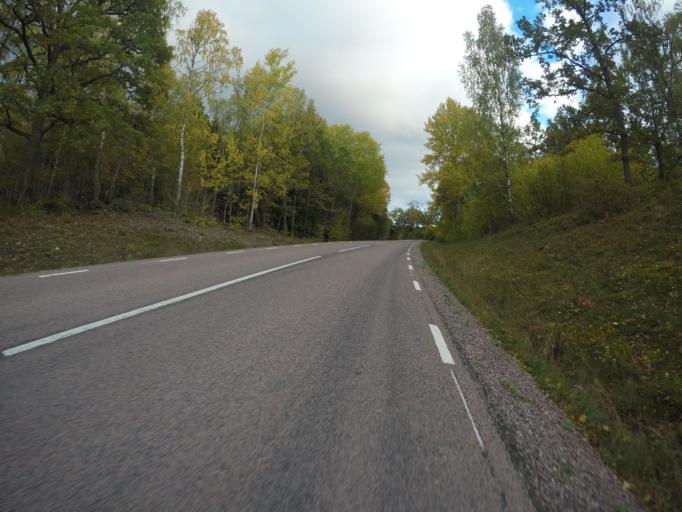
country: SE
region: Vaestmanland
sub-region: Arboga Kommun
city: Tyringe
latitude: 59.3144
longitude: 15.9816
